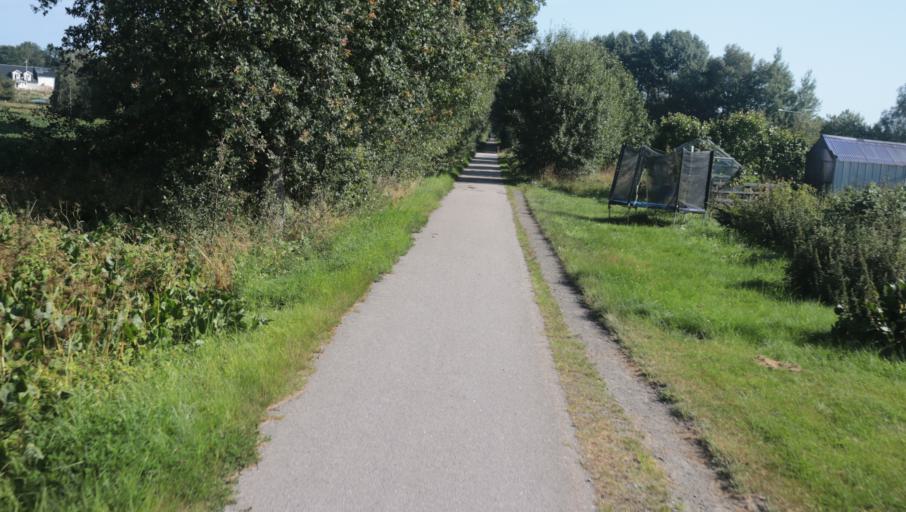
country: SE
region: Blekinge
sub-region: Karlshamns Kommun
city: Svangsta
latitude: 56.2308
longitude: 14.8114
